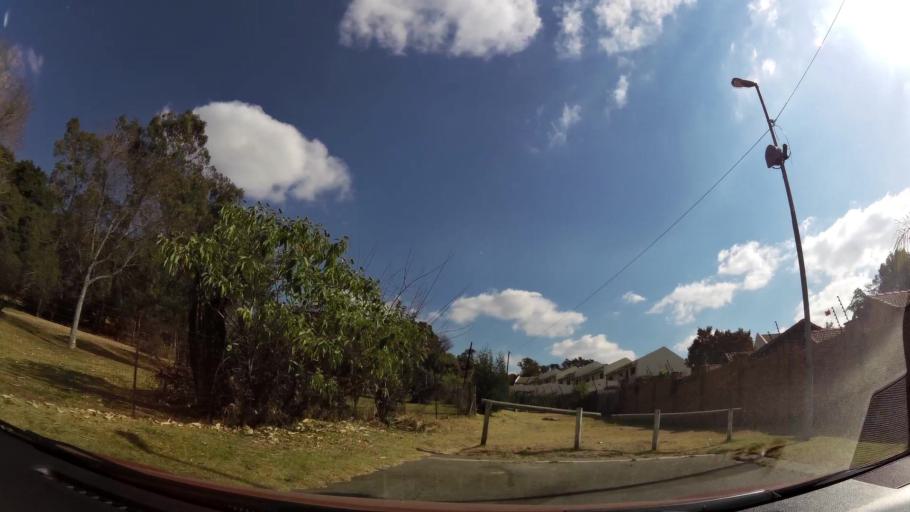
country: ZA
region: Gauteng
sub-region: West Rand District Municipality
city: Muldersdriseloop
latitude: -26.0653
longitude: 27.9563
